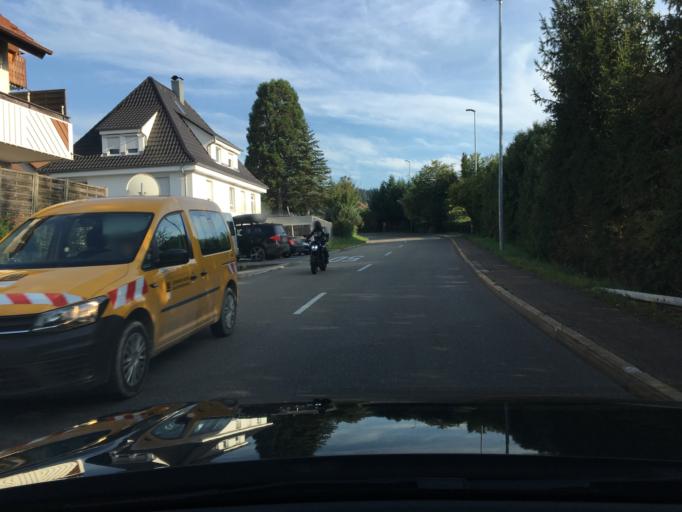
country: DE
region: Baden-Wuerttemberg
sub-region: Regierungsbezirk Stuttgart
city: Schorndorf
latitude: 48.8005
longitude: 9.5406
